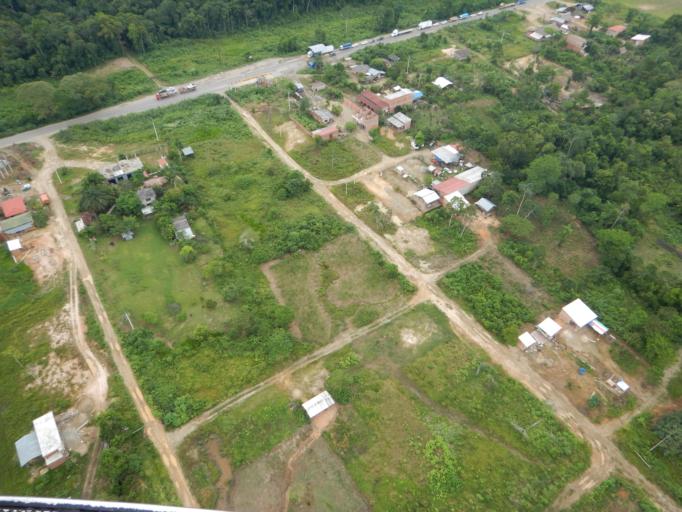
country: BO
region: Cochabamba
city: Chimore
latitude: -17.0268
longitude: -64.8808
